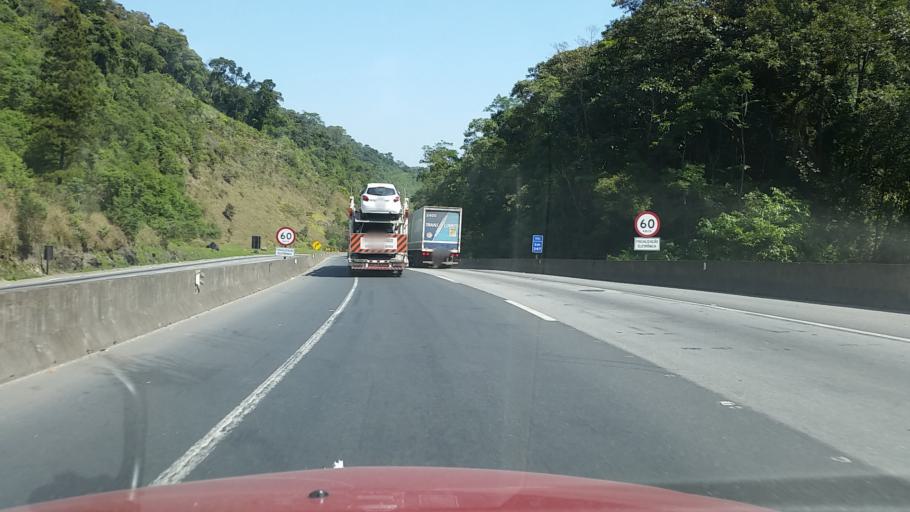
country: BR
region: Sao Paulo
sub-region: Juquitiba
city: Juquitiba
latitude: -24.0469
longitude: -47.1977
